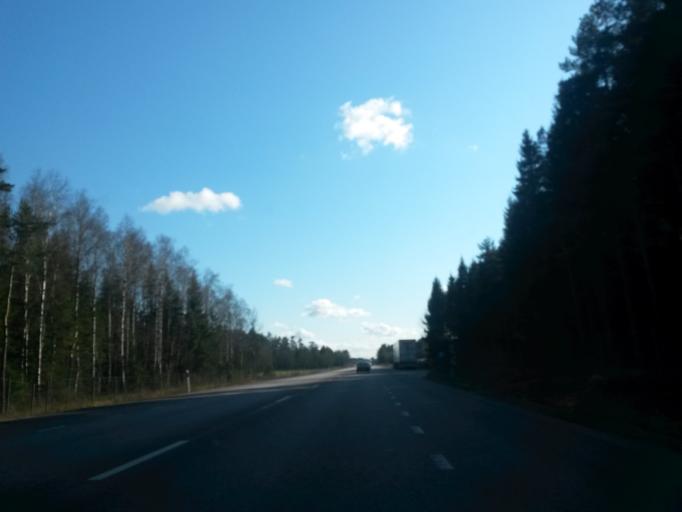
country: SE
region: Vaestra Goetaland
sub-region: Vara Kommun
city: Vara
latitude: 58.1811
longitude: 12.8955
